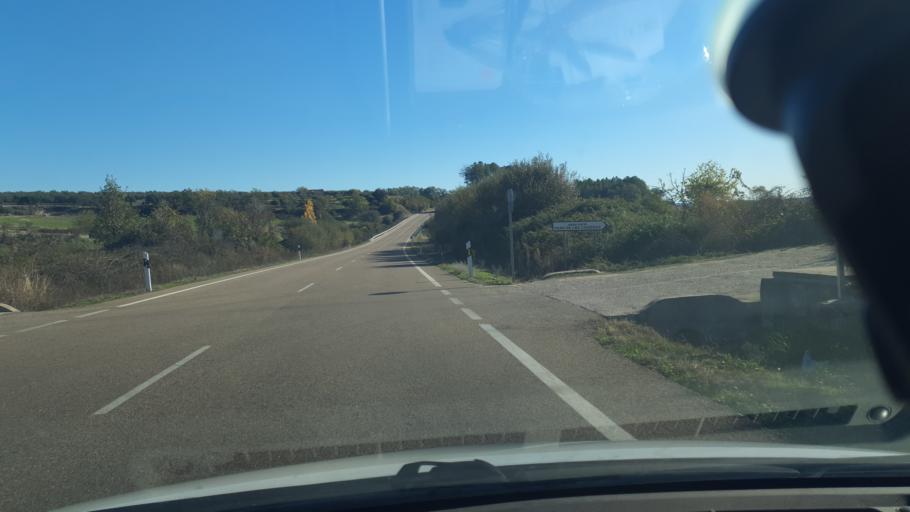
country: ES
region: Castille and Leon
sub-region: Provincia de Avila
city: Candeleda
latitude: 40.1373
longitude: -5.2421
